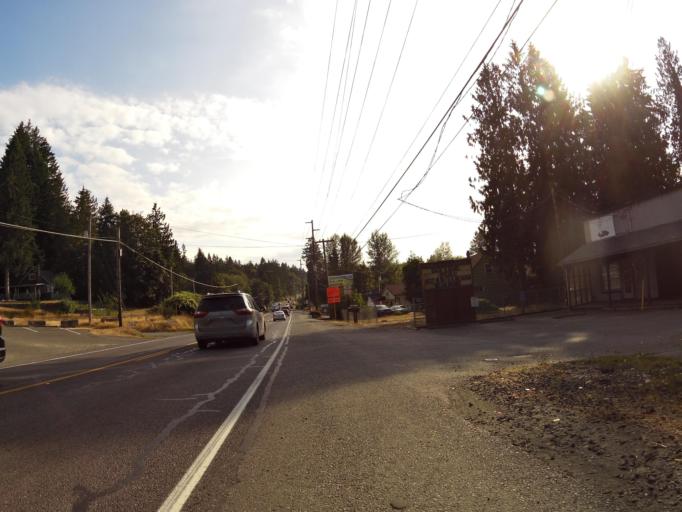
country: US
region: Washington
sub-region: Mason County
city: Belfair
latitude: 47.4354
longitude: -122.8390
